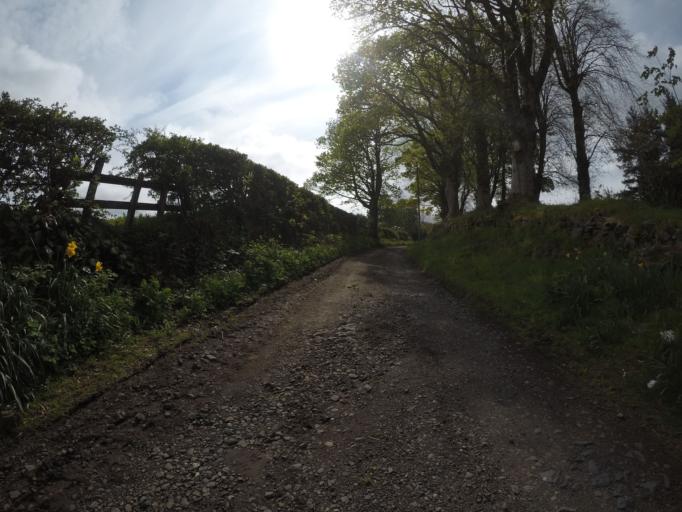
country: GB
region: Scotland
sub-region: East Renfrewshire
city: Newton Mearns
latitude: 55.7575
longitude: -4.3280
